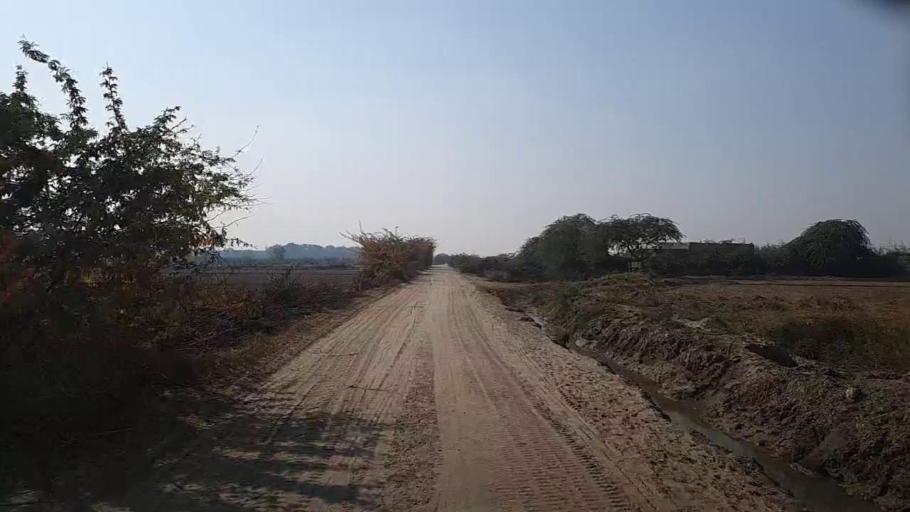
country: PK
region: Sindh
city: Bozdar
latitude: 27.2406
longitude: 68.6014
